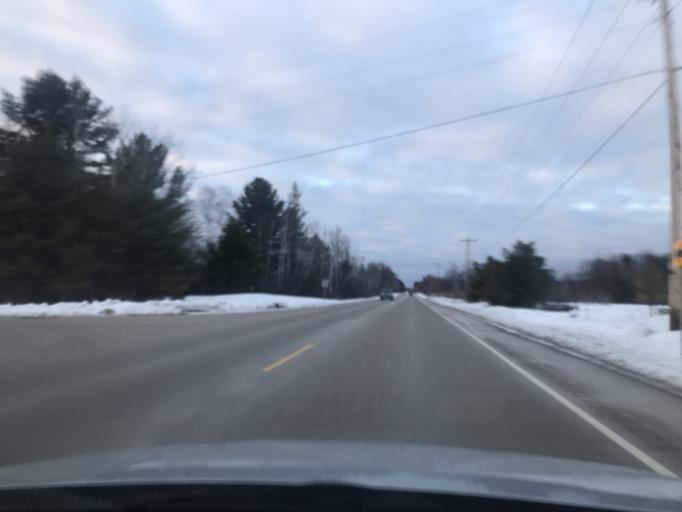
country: US
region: Wisconsin
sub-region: Marinette County
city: Marinette
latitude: 45.1212
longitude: -87.6829
